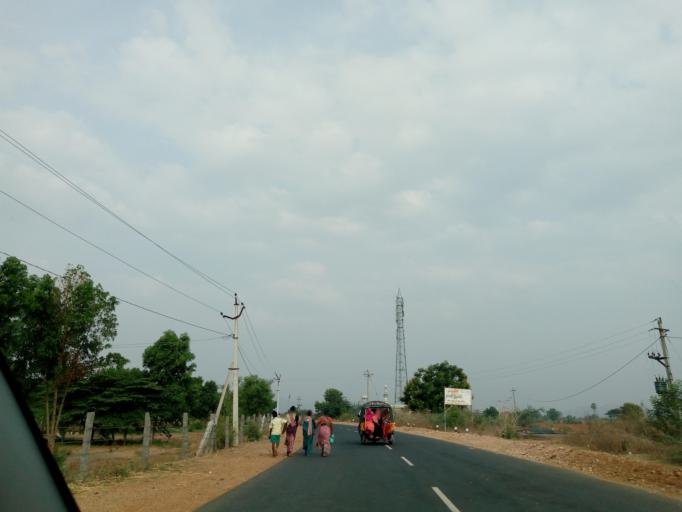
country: IN
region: Andhra Pradesh
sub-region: Prakasam
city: Diguvametta
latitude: 15.3740
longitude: 78.8764
